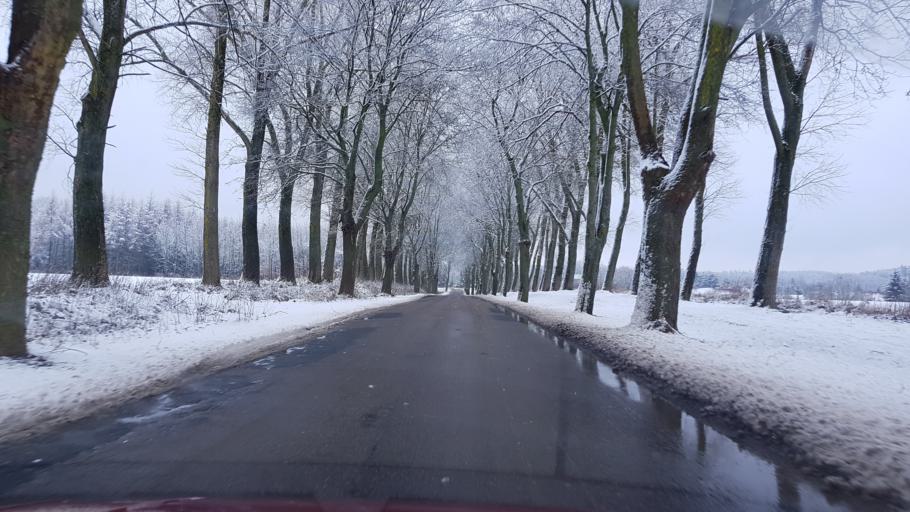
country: PL
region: West Pomeranian Voivodeship
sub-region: Powiat drawski
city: Zlocieniec
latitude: 53.5379
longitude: 16.0446
